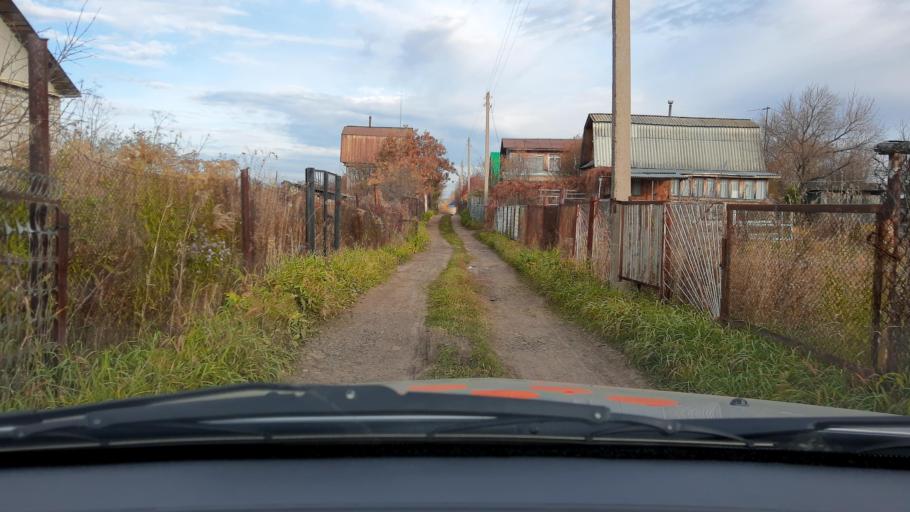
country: RU
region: Bashkortostan
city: Asanovo
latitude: 54.8047
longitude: 55.6126
